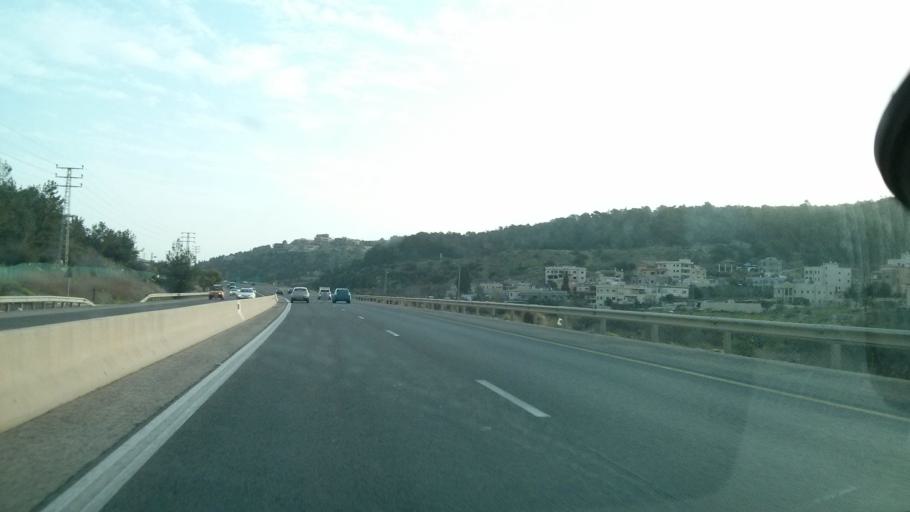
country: PS
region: West Bank
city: Barta`ah ash Sharqiyah
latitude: 32.5096
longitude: 35.1124
